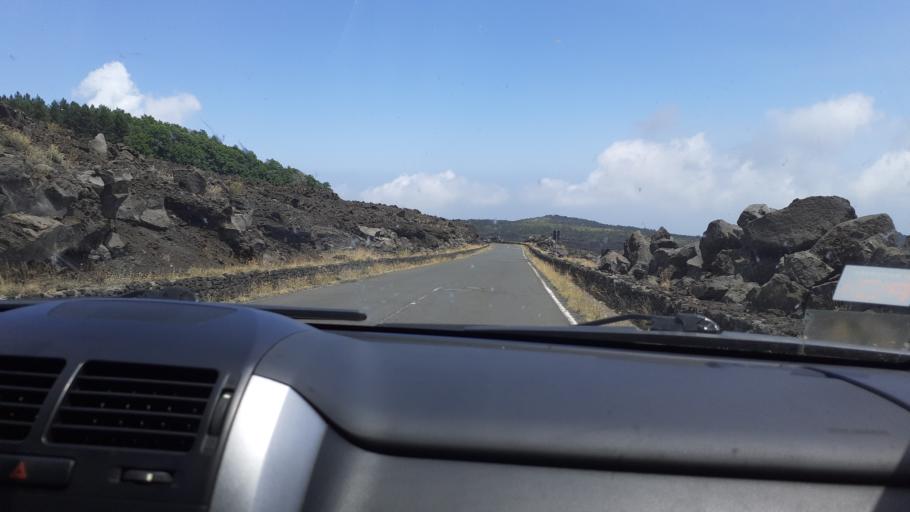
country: IT
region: Sicily
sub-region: Catania
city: Nicolosi
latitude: 37.6859
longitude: 15.0190
